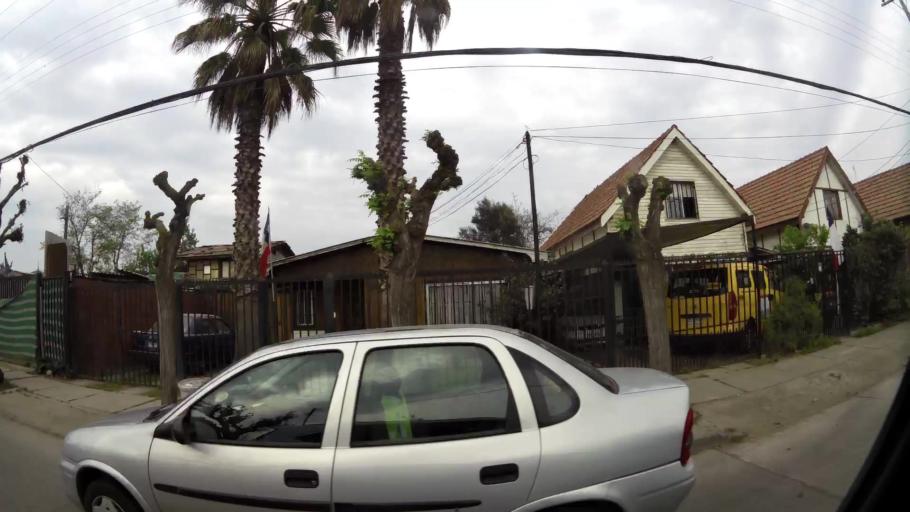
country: CL
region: Santiago Metropolitan
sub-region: Provincia de Santiago
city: Lo Prado
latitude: -33.5088
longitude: -70.7657
